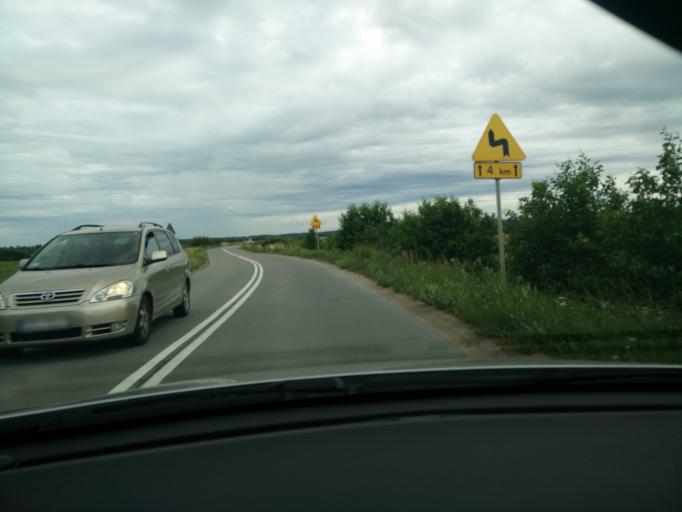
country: PL
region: Pomeranian Voivodeship
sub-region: Powiat pucki
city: Mrzezino
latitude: 54.6470
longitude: 18.4355
